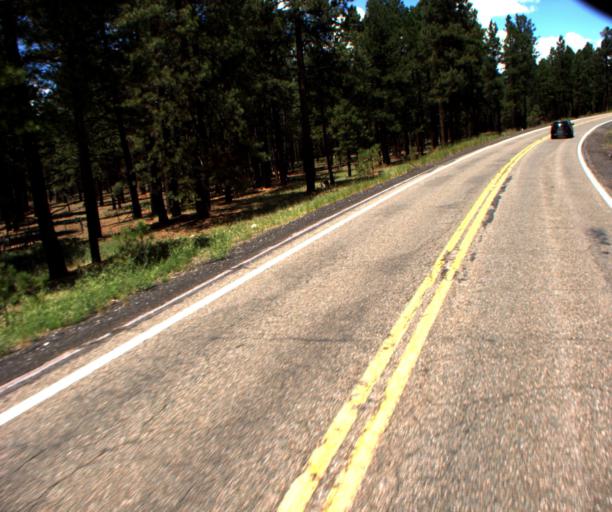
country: US
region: Arizona
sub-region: Coconino County
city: Flagstaff
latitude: 35.2957
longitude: -111.7654
